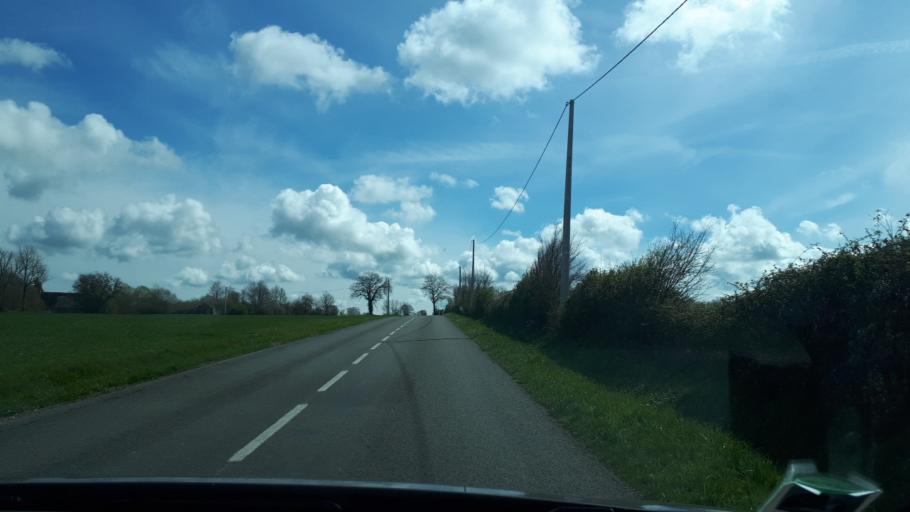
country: FR
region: Pays de la Loire
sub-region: Departement de la Sarthe
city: Bouloire
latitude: 47.8984
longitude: 0.5868
